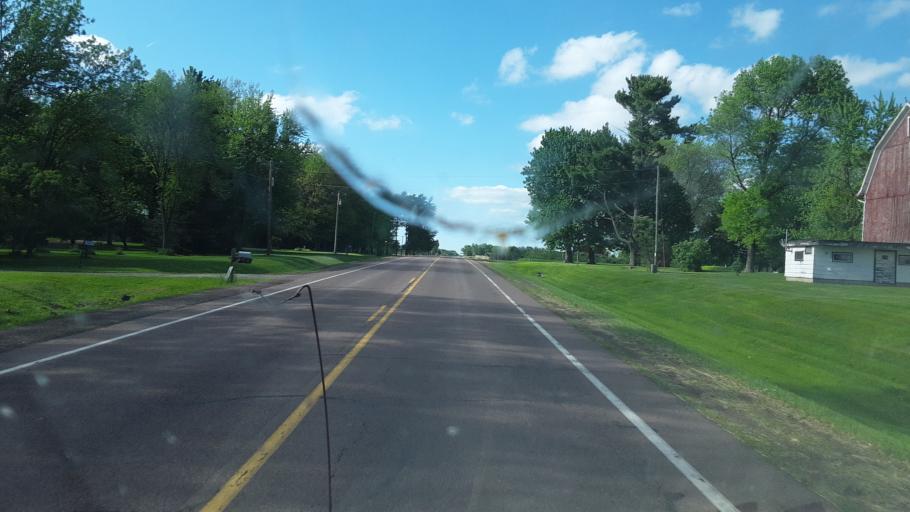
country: US
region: Wisconsin
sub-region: Wood County
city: Marshfield
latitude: 44.5748
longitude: -90.1807
